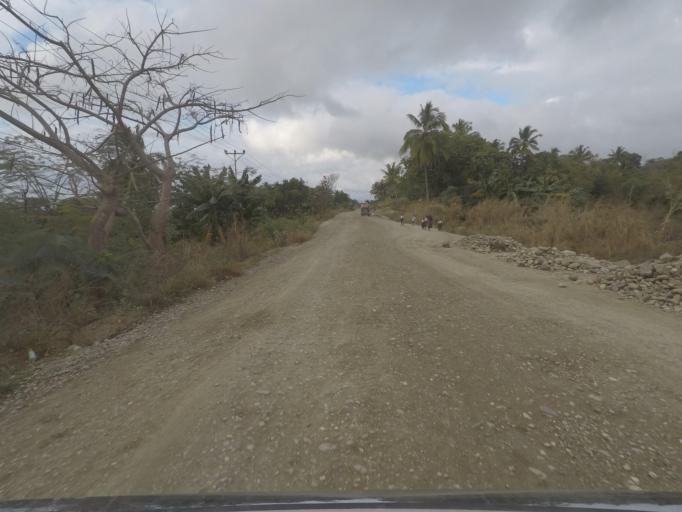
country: TL
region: Baucau
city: Baucau
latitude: -8.5090
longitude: 126.4434
